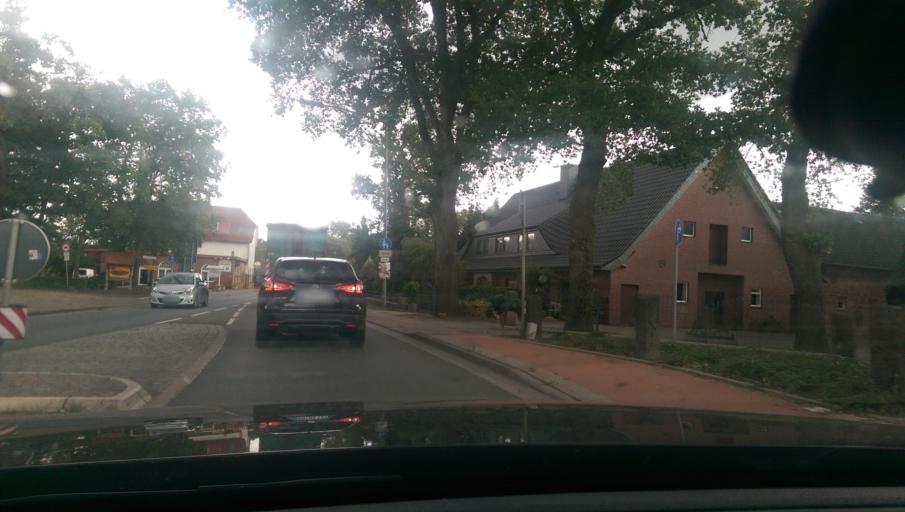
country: DE
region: Lower Saxony
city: Kirchseelte
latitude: 52.9974
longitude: 8.7067
